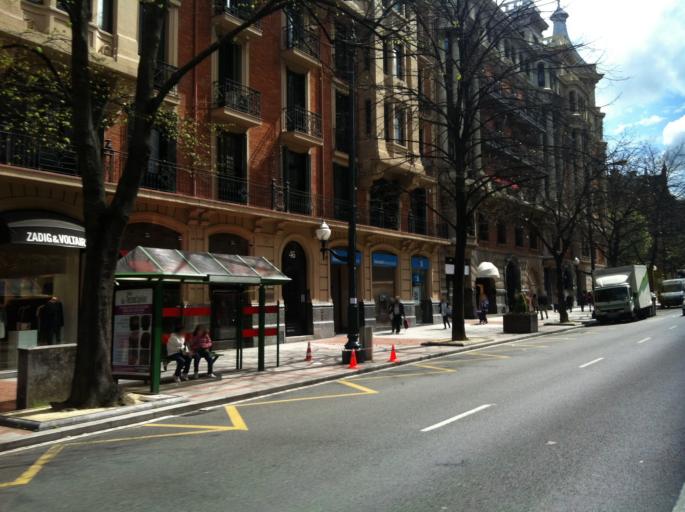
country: ES
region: Basque Country
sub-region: Bizkaia
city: Bilbao
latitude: 43.2636
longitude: -2.9373
